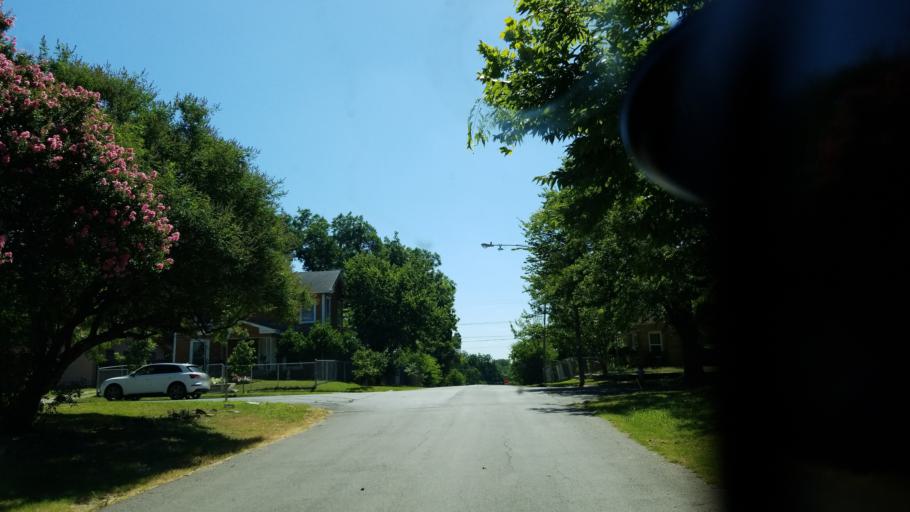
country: US
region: Texas
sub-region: Dallas County
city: Dallas
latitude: 32.7114
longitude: -96.8125
